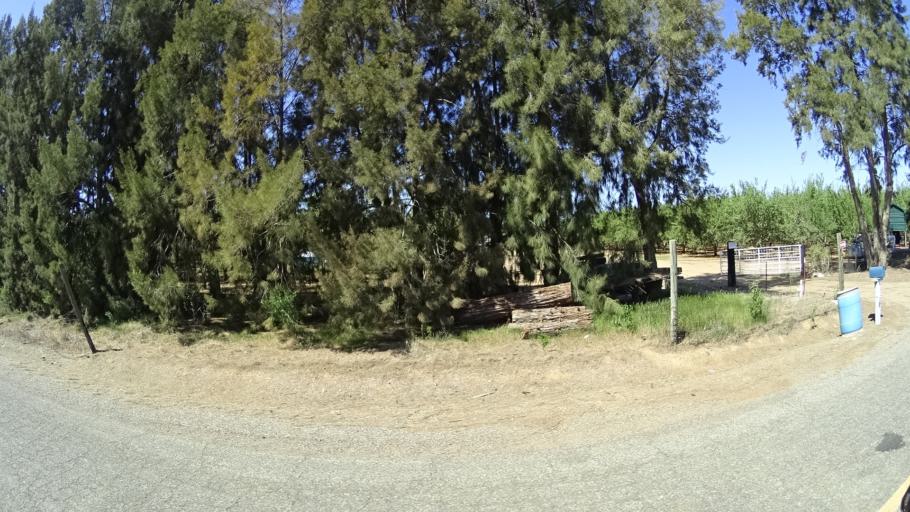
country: US
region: California
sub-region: Glenn County
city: Orland
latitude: 39.6789
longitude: -122.2531
